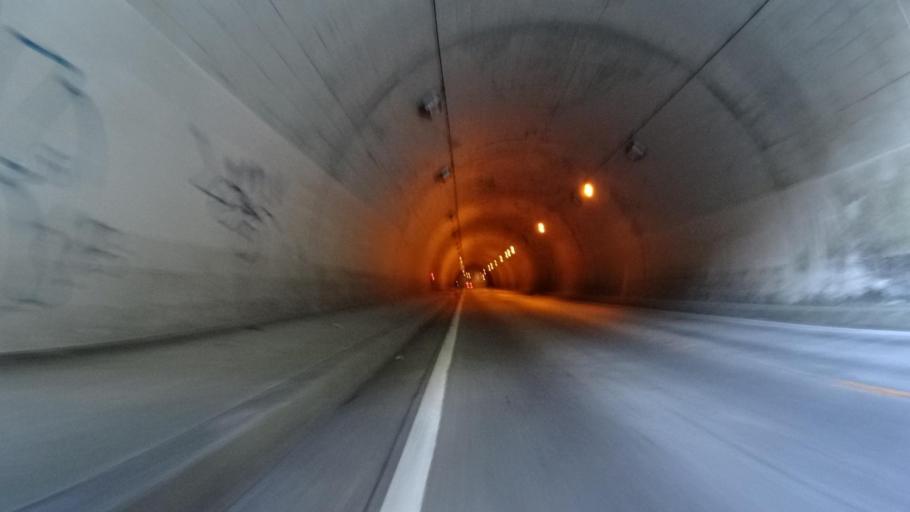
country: JP
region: Tokyo
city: Hachioji
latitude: 35.5366
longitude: 139.2544
